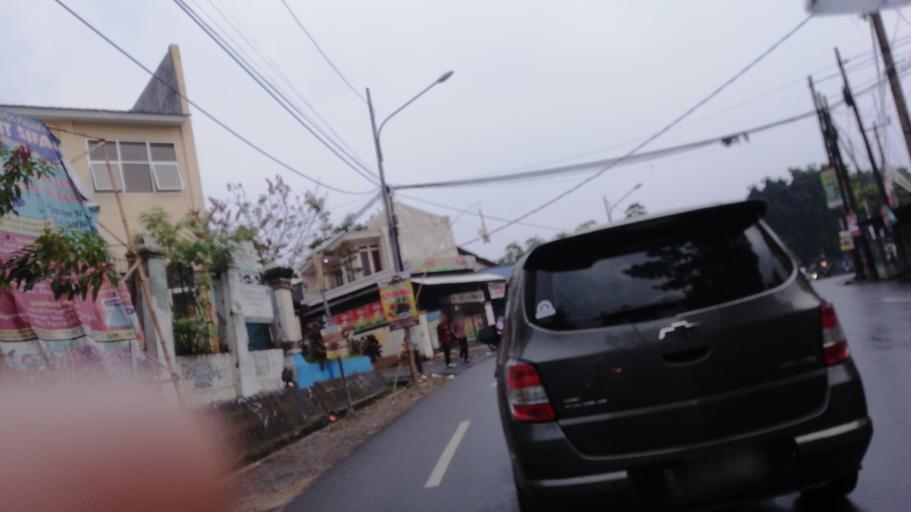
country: ID
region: West Java
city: Cibinong
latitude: -6.5244
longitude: 106.8087
